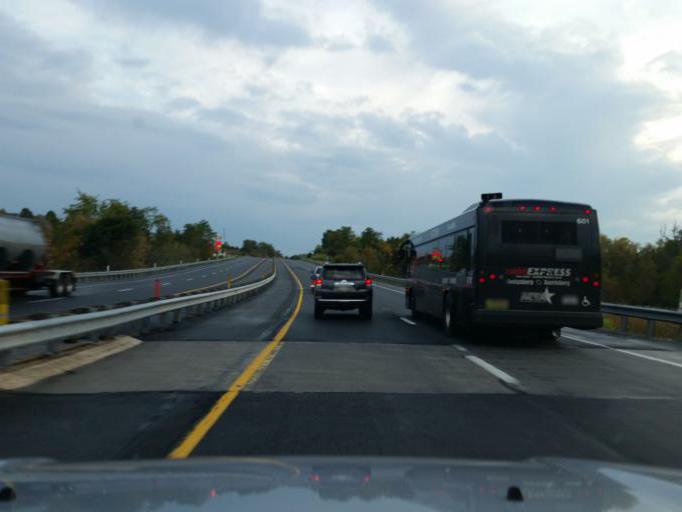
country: US
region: Pennsylvania
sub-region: Adams County
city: Lake Meade
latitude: 40.0095
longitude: -77.1021
